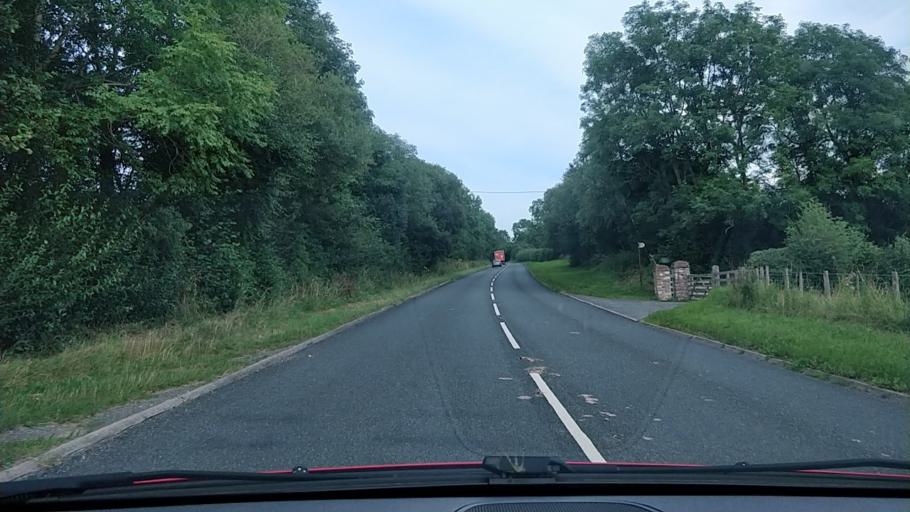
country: GB
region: Wales
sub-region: Denbighshire
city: Corwen
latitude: 52.9977
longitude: -3.3651
